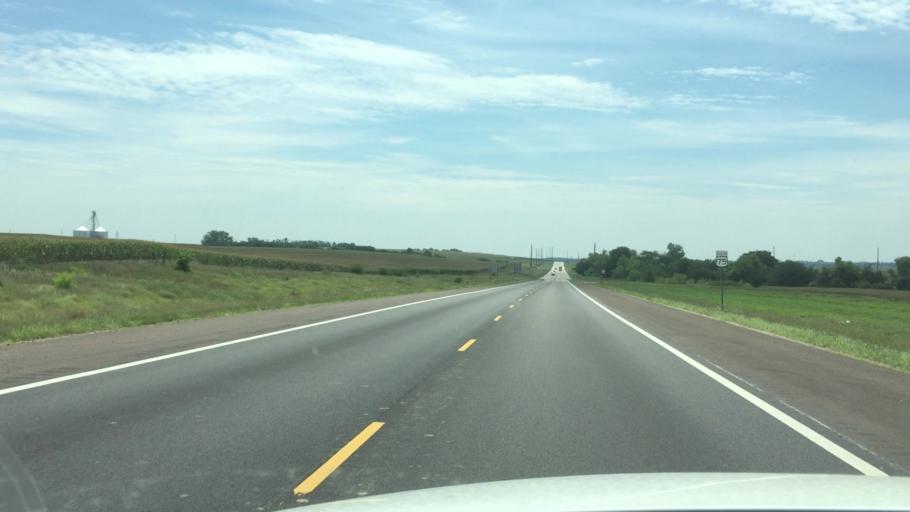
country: US
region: Kansas
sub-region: Nemaha County
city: Sabetha
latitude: 39.8343
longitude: -95.7337
